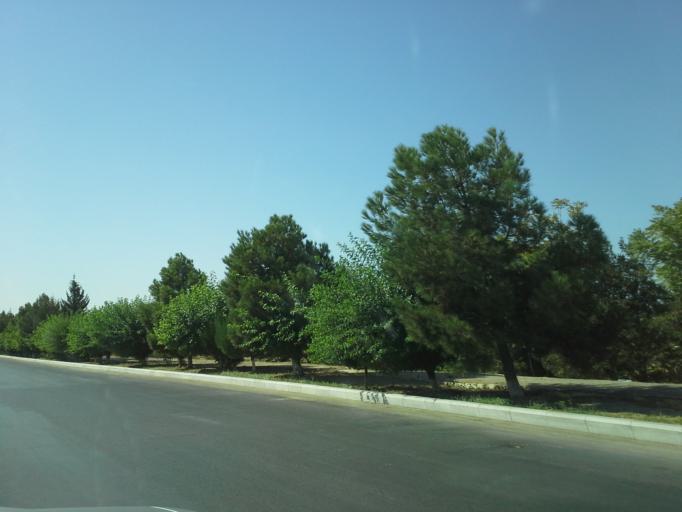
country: TM
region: Ahal
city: Annau
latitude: 37.9177
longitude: 58.4624
